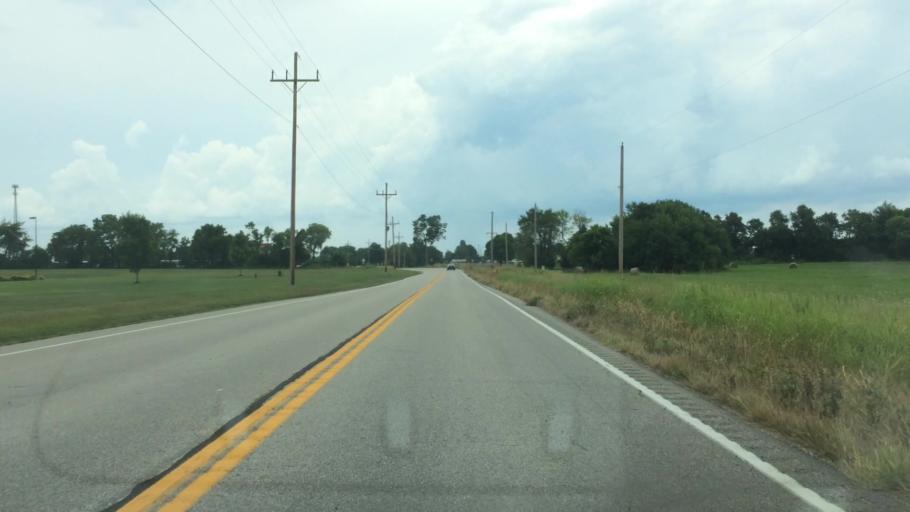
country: US
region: Missouri
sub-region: Greene County
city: Strafford
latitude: 37.2601
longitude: -93.1351
